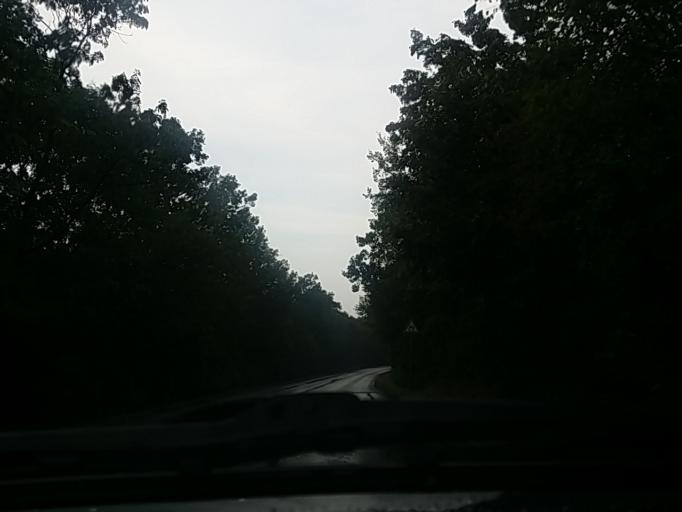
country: HU
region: Pest
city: Paty
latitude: 47.5007
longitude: 18.8723
